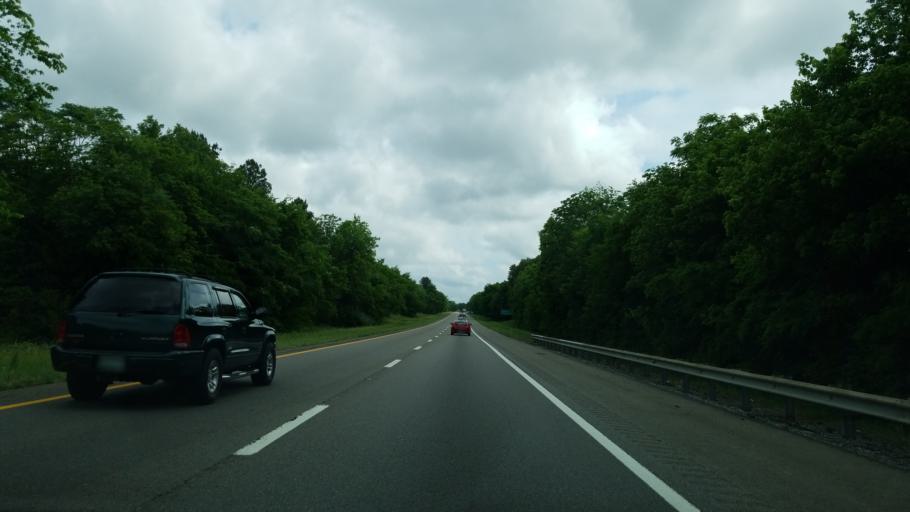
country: US
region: Tennessee
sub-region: Loudon County
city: Loudon
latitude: 35.7057
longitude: -84.4212
